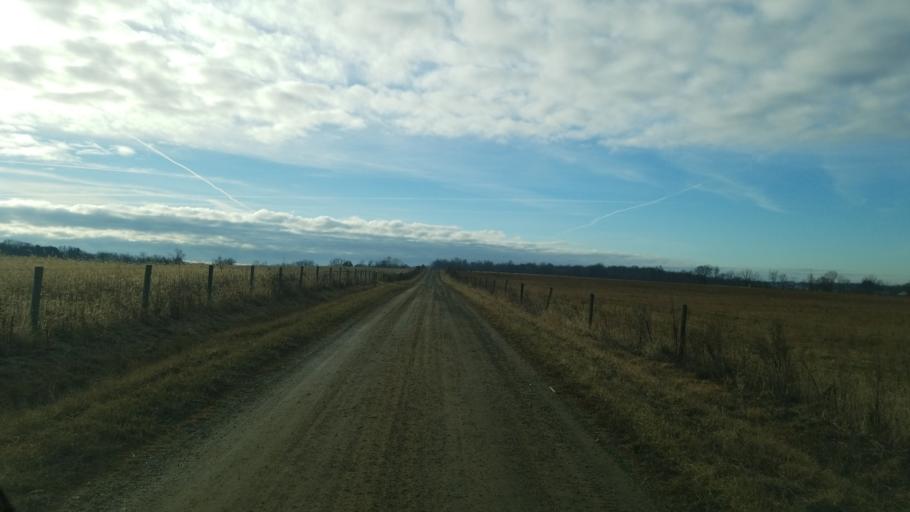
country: US
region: Ohio
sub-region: Knox County
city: Gambier
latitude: 40.3230
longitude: -82.3210
